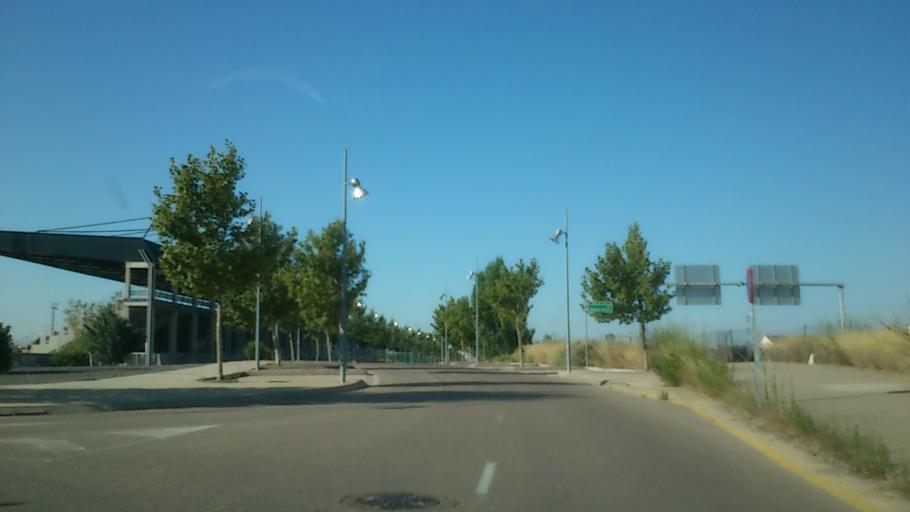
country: ES
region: Aragon
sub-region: Provincia de Zaragoza
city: Villanueva de Gallego
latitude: 41.7599
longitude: -0.8336
